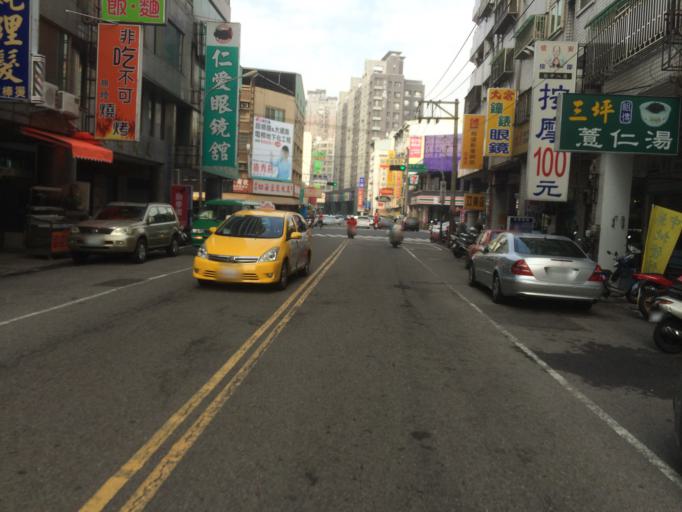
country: TW
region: Taiwan
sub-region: Taichung City
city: Taichung
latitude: 24.1754
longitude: 120.6910
